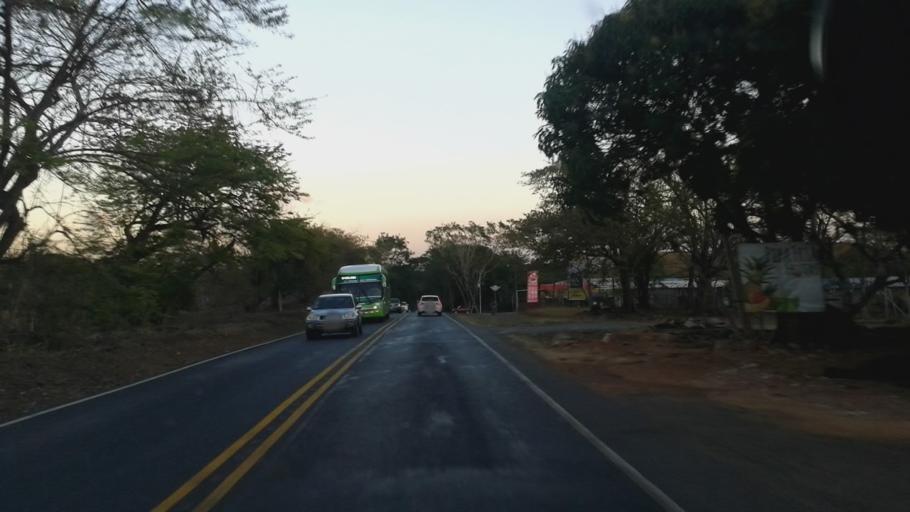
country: CR
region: Puntarenas
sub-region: Canton Central de Puntarenas
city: Puntarenas
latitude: 10.1115
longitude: -84.8906
